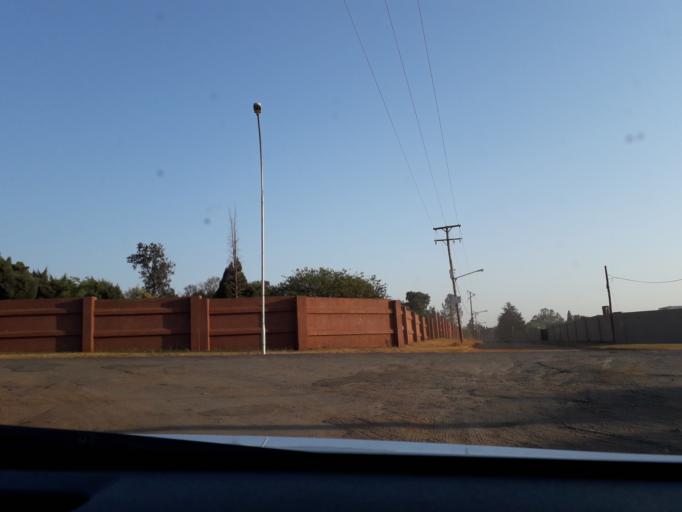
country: ZA
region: Gauteng
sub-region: Ekurhuleni Metropolitan Municipality
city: Benoni
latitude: -26.1101
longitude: 28.3019
